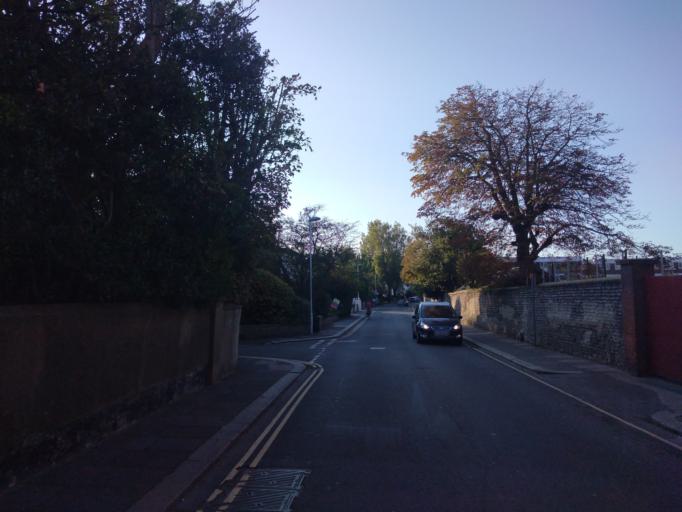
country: GB
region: England
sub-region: West Sussex
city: Worthing
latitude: 50.8130
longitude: -0.3768
